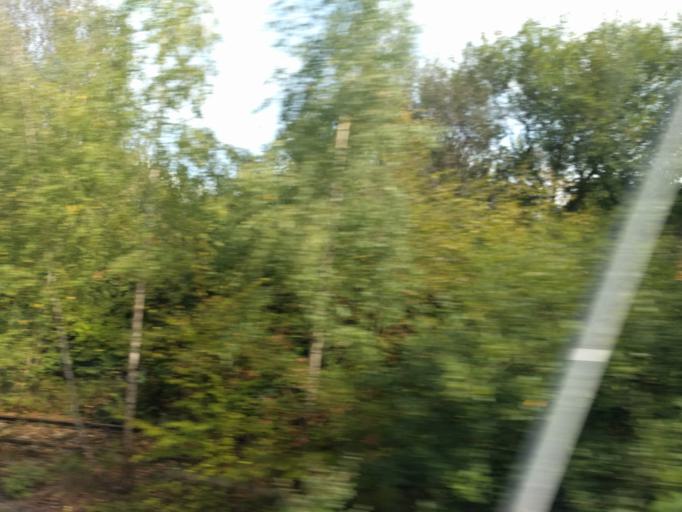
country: DE
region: Schleswig-Holstein
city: Delingsdorf
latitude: 53.6889
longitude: 10.2520
